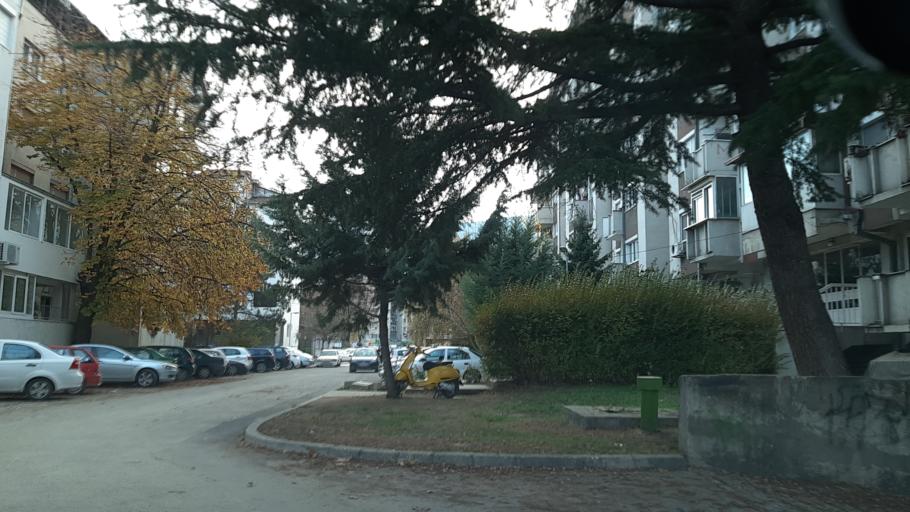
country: MK
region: Karpos
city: Skopje
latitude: 41.9825
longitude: 21.4430
